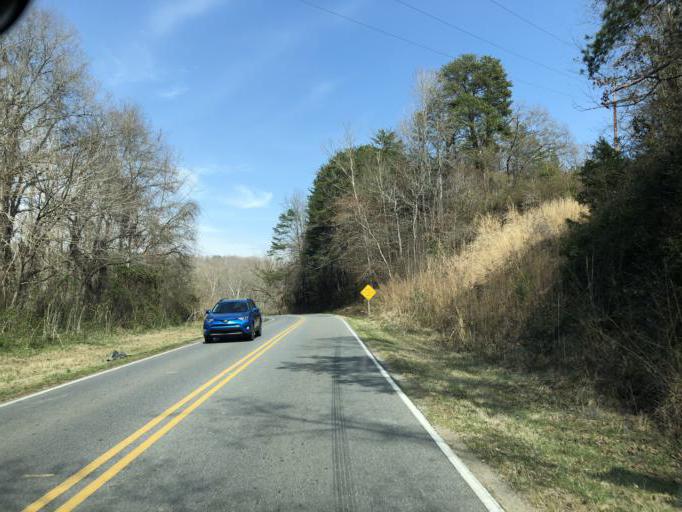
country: US
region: North Carolina
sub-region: Gaston County
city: Ranlo
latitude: 35.3067
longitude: -81.1075
